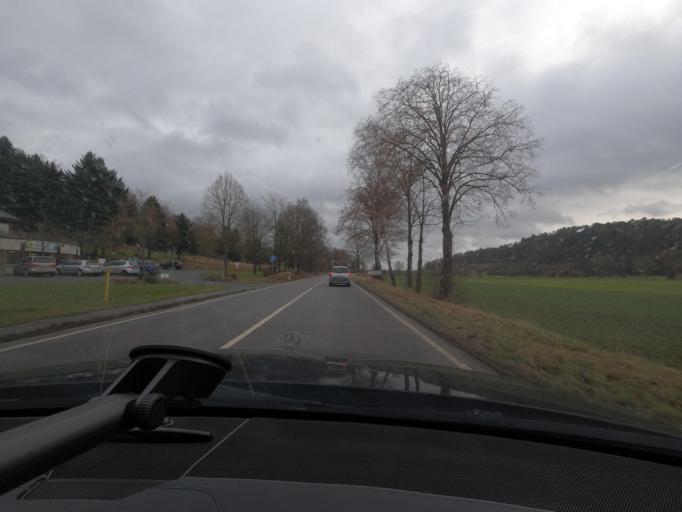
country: DE
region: Hesse
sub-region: Regierungsbezirk Kassel
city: Volkmarsen
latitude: 51.4056
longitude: 9.1373
